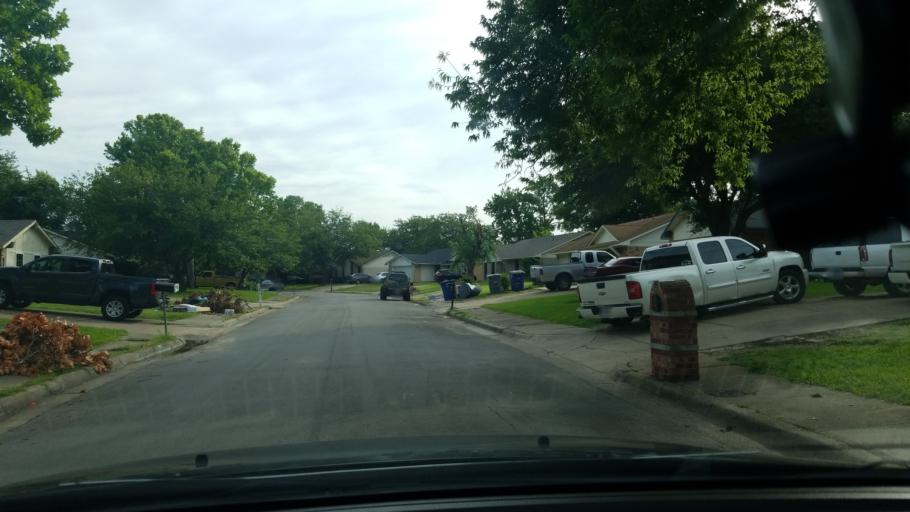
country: US
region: Texas
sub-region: Dallas County
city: Balch Springs
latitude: 32.7539
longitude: -96.6552
